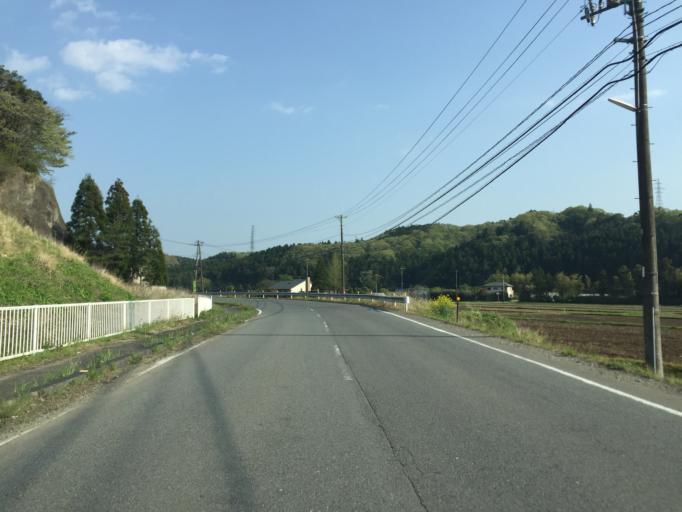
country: JP
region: Fukushima
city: Iwaki
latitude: 36.9583
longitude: 140.8199
